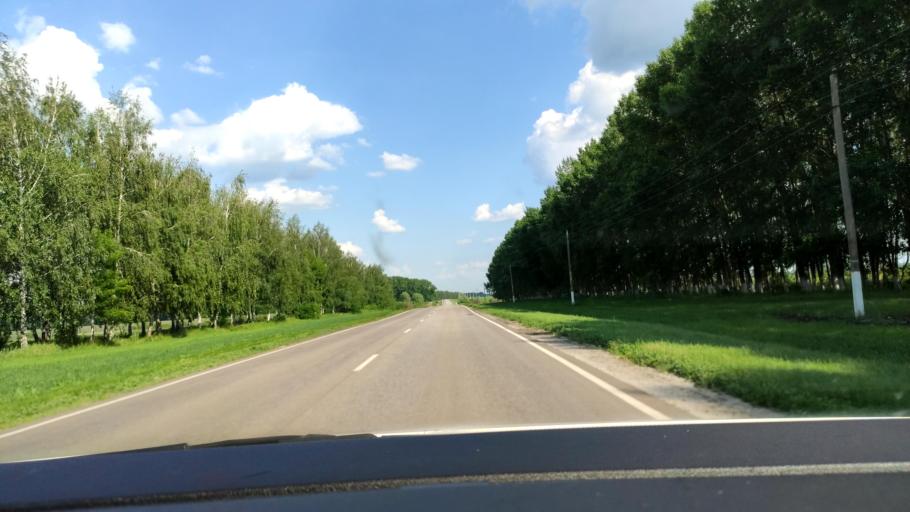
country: RU
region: Voronezj
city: Panino
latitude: 51.6590
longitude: 39.9913
